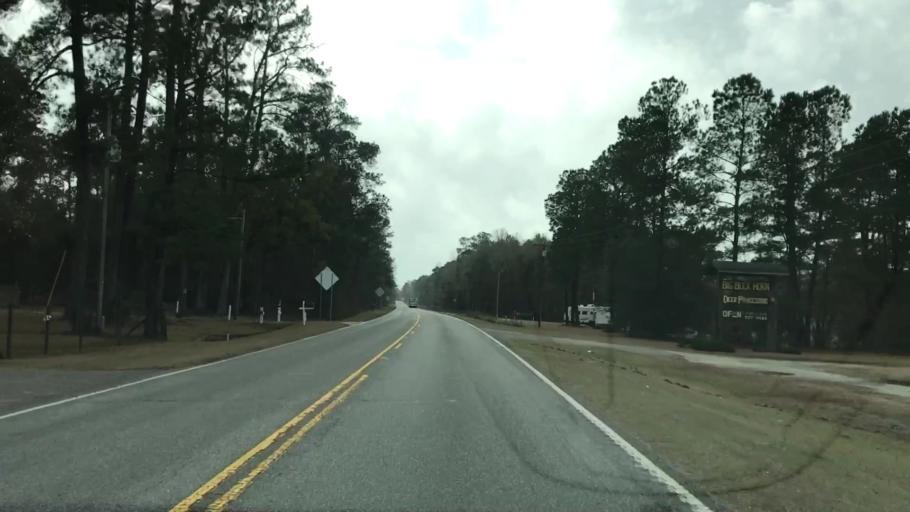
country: US
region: South Carolina
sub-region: Georgetown County
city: Murrells Inlet
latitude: 33.6495
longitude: -79.1697
